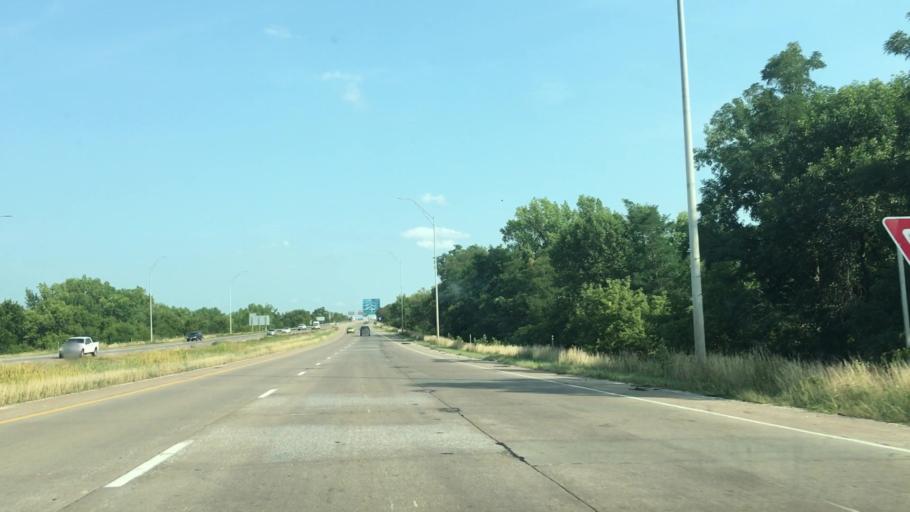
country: US
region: Illinois
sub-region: Rock Island County
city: Rock Island
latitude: 41.4886
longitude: -90.6451
